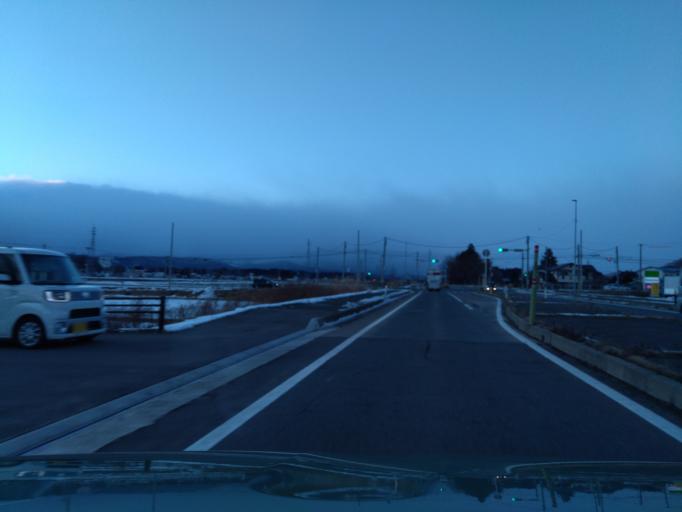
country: JP
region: Iwate
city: Shizukuishi
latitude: 39.6980
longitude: 140.9776
